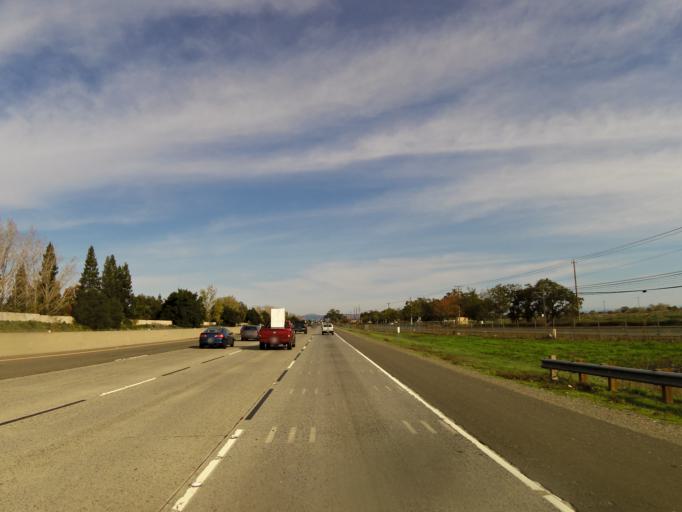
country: US
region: California
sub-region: Sacramento County
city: Gold River
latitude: 38.6179
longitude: -121.2466
